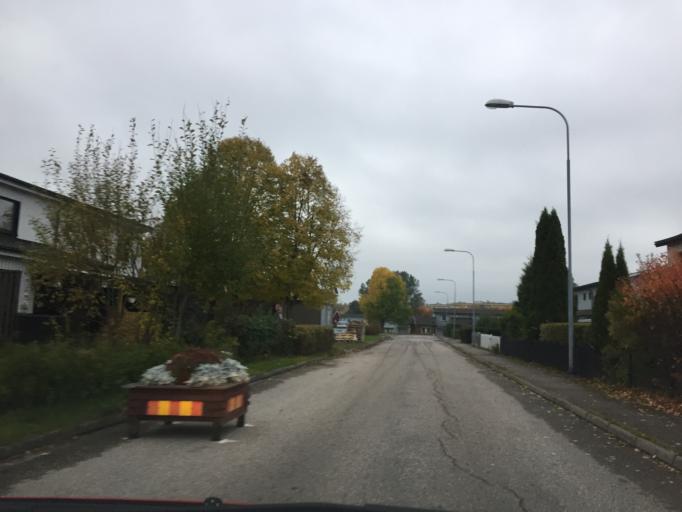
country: SE
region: Vaestra Goetaland
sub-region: Trollhattan
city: Trollhattan
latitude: 58.2572
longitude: 12.3009
